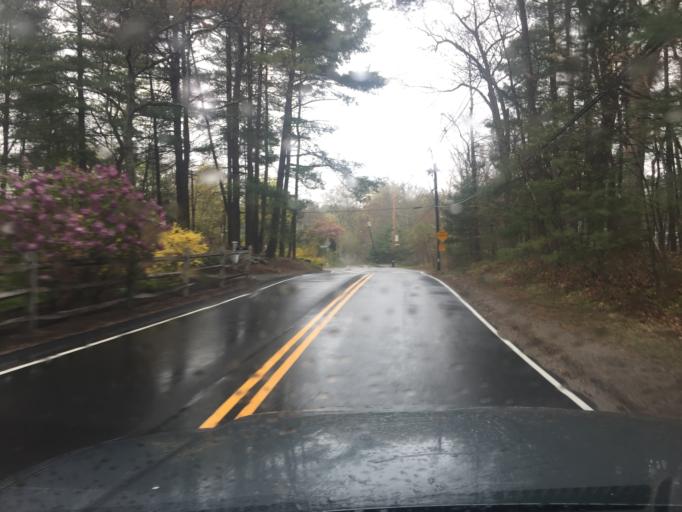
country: US
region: Massachusetts
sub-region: Norfolk County
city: Westwood
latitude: 42.2326
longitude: -71.2248
